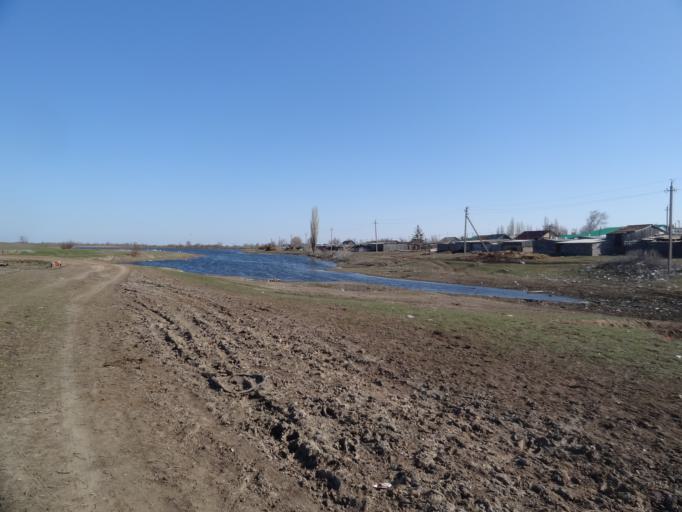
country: RU
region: Saratov
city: Shumeyka
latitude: 51.3916
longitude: 46.2919
